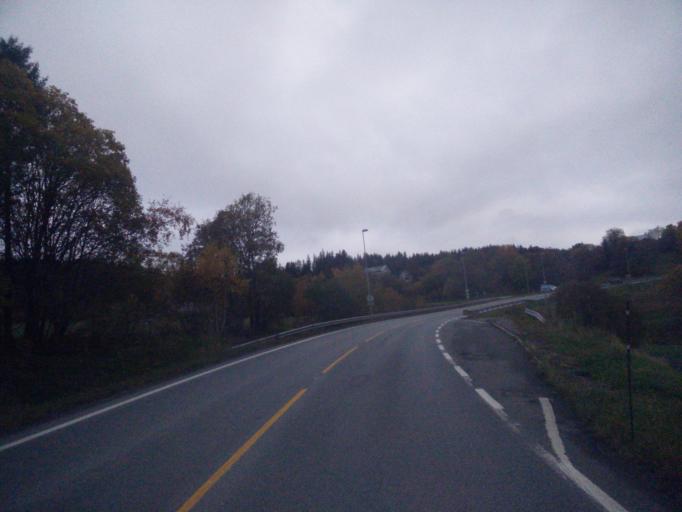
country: NO
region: Nord-Trondelag
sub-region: Stjordal
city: Stjordal
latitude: 63.5087
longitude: 10.8530
